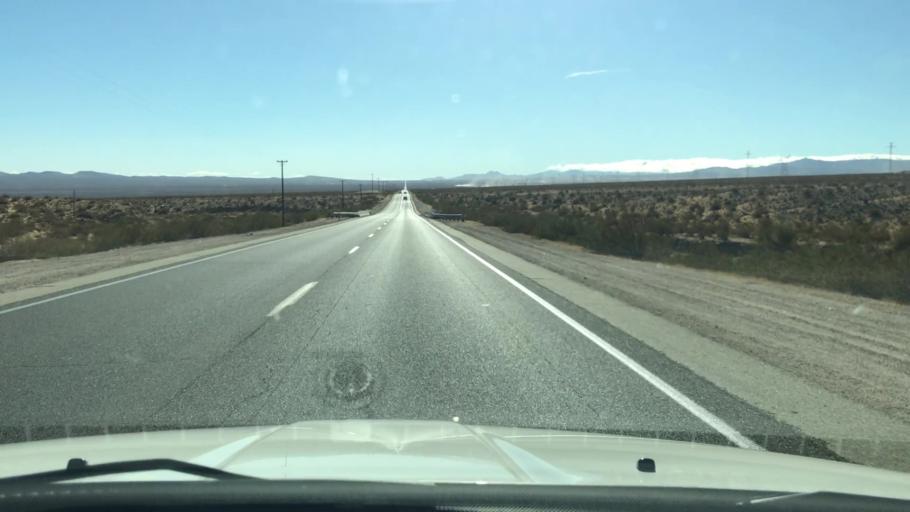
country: US
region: California
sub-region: Kern County
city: Inyokern
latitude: 35.5836
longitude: -117.9116
